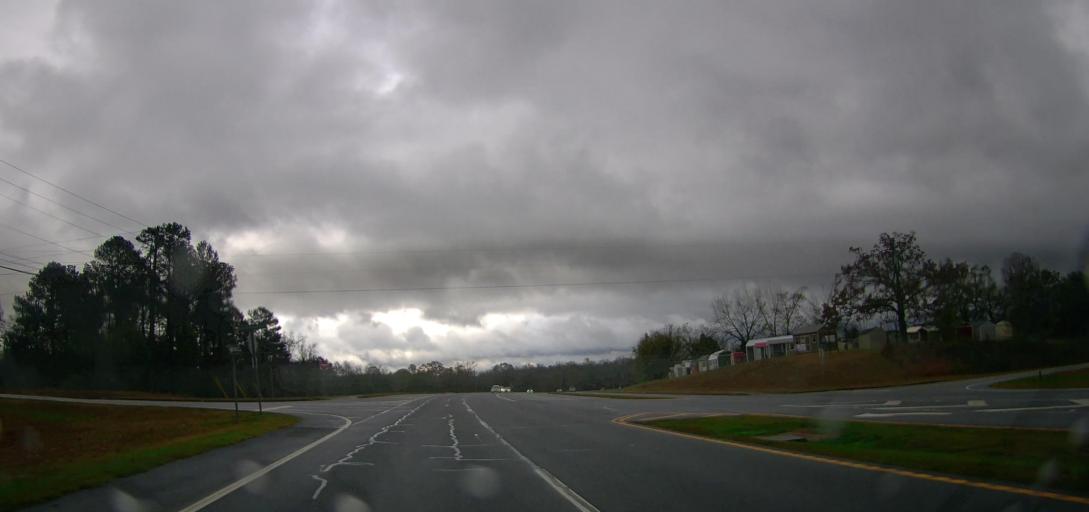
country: US
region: Georgia
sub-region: Jackson County
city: Nicholson
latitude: 34.1334
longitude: -83.4290
